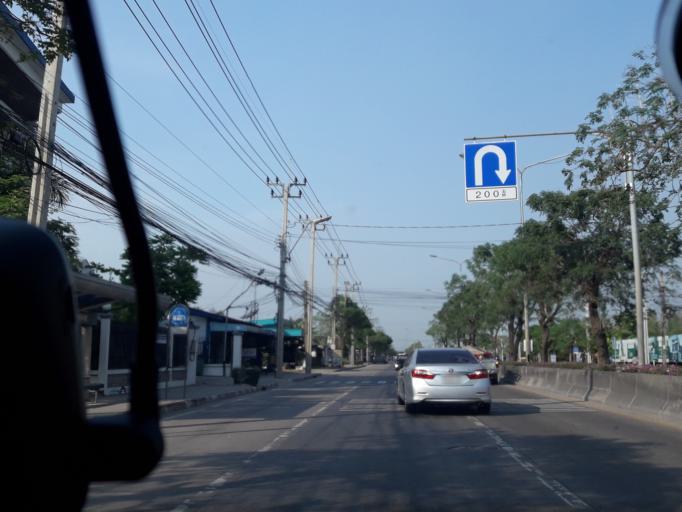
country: TH
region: Bangkok
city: Khlong Sam Wa
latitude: 13.8831
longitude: 100.7317
